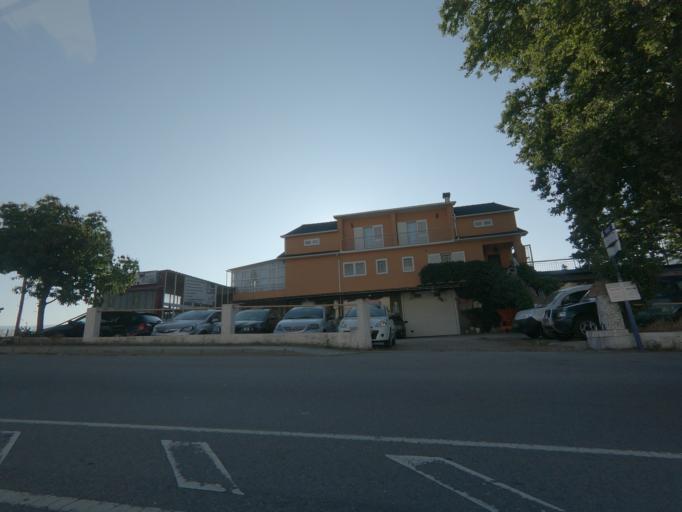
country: PT
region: Vila Real
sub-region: Vila Real
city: Vila Real
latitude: 41.3091
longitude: -7.7257
